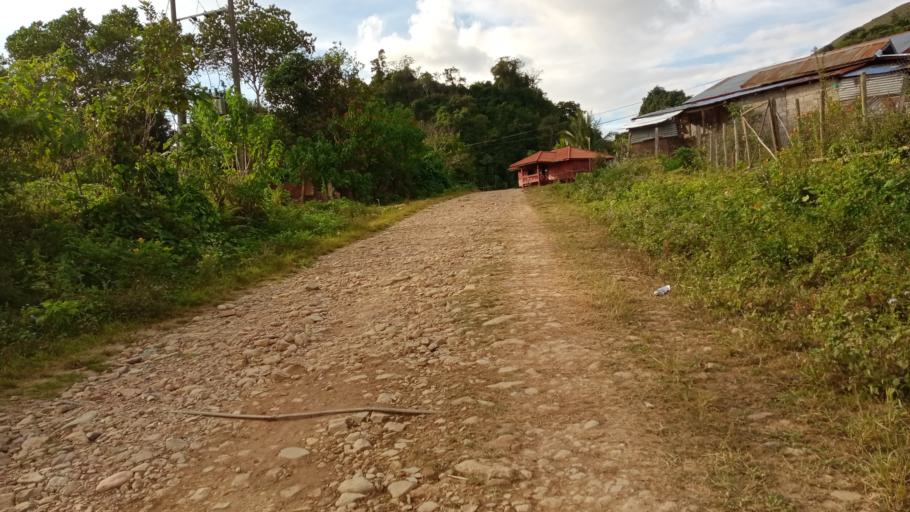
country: LA
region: Xiangkhoang
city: Phonsavan
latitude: 19.1098
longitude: 102.9254
